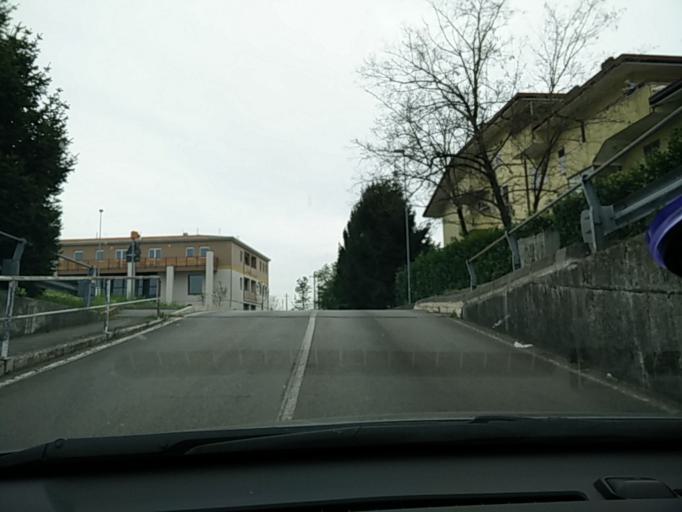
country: IT
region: Veneto
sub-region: Provincia di Treviso
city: San Floriano-Olmi
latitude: 45.6759
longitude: 12.3368
